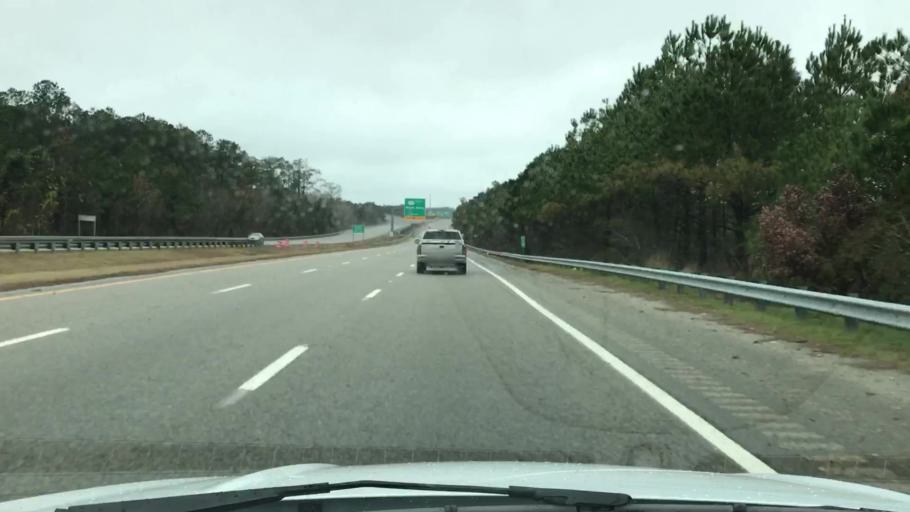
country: US
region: South Carolina
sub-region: Horry County
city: Forestbrook
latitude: 33.7422
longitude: -78.9397
